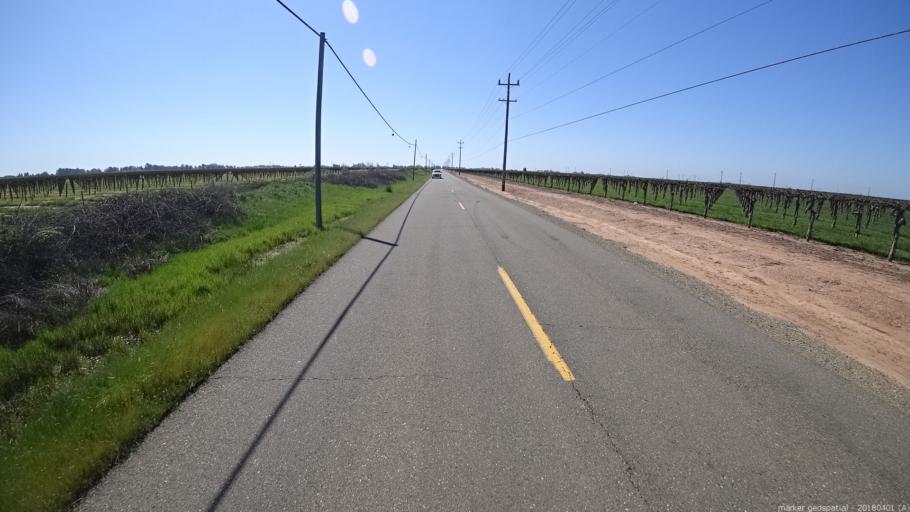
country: US
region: California
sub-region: Sacramento County
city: Wilton
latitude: 38.3711
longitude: -121.2421
